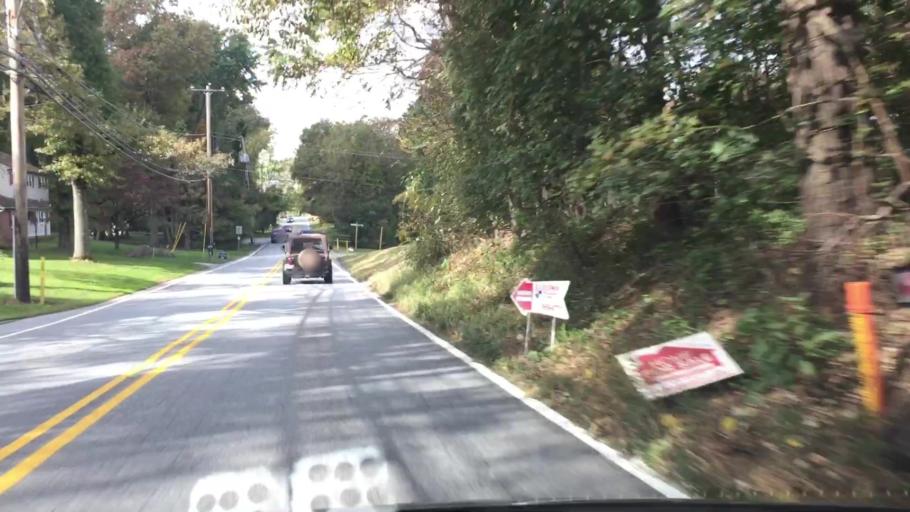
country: US
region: Pennsylvania
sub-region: Chester County
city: West Chester
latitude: 39.9931
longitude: -75.5586
